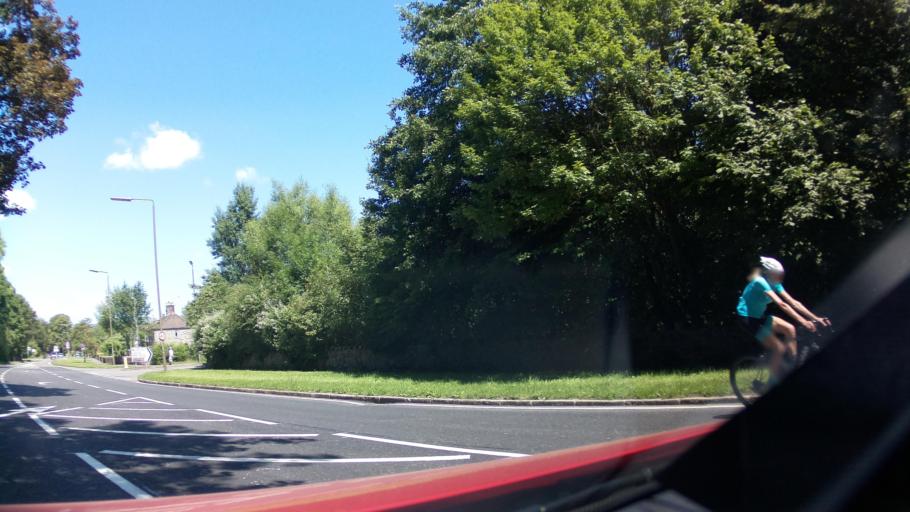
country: GB
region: England
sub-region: Derbyshire
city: Bakewell
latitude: 53.2059
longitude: -1.6673
